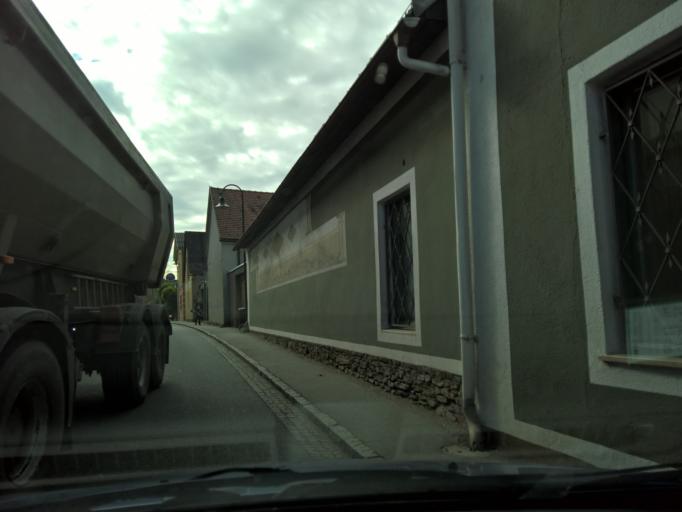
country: AT
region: Styria
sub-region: Politischer Bezirk Leibnitz
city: Grossklein
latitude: 46.7369
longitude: 15.4420
